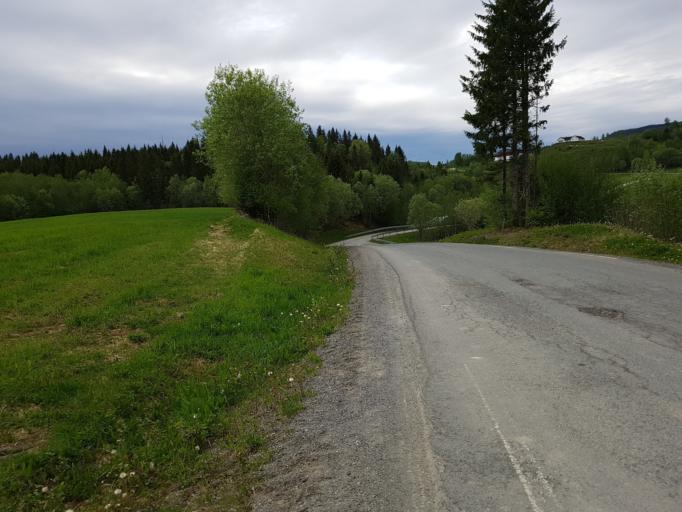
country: NO
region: Nord-Trondelag
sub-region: Levanger
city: Skogn
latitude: 63.6305
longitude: 11.2766
